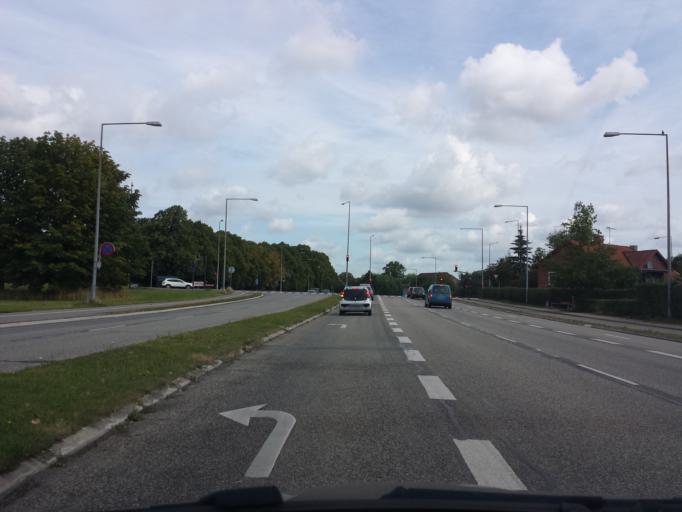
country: DK
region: Capital Region
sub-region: Rodovre Kommune
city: Rodovre
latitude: 55.7006
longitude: 12.4511
